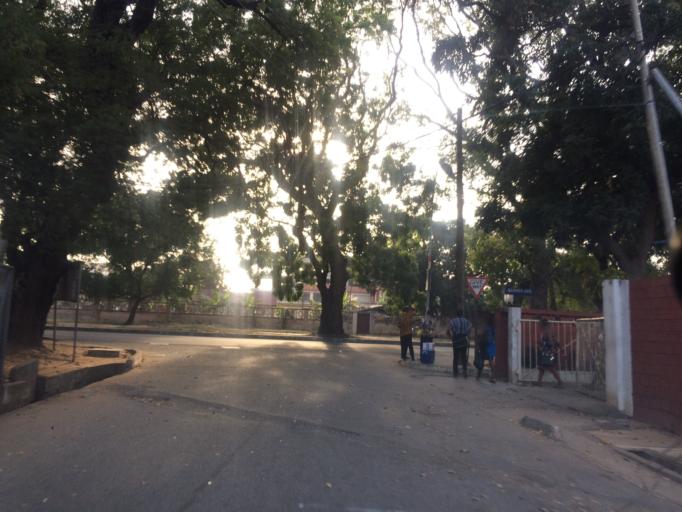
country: GH
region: Greater Accra
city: Accra
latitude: 5.5593
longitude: -0.2054
